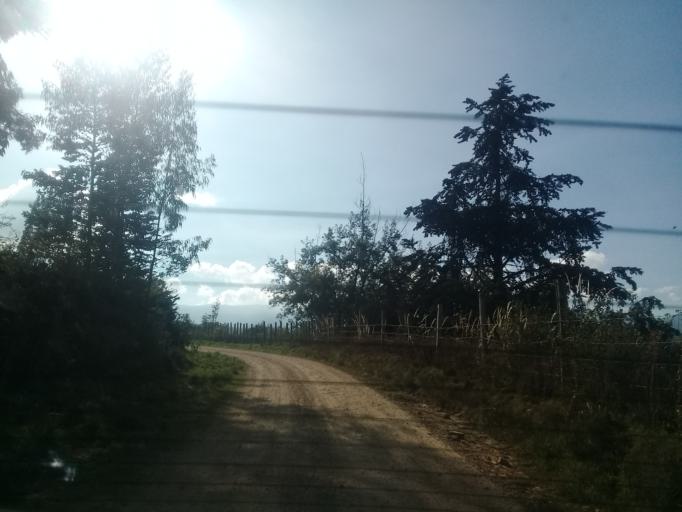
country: CO
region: Cundinamarca
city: Guatavita
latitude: 4.9417
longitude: -73.8654
